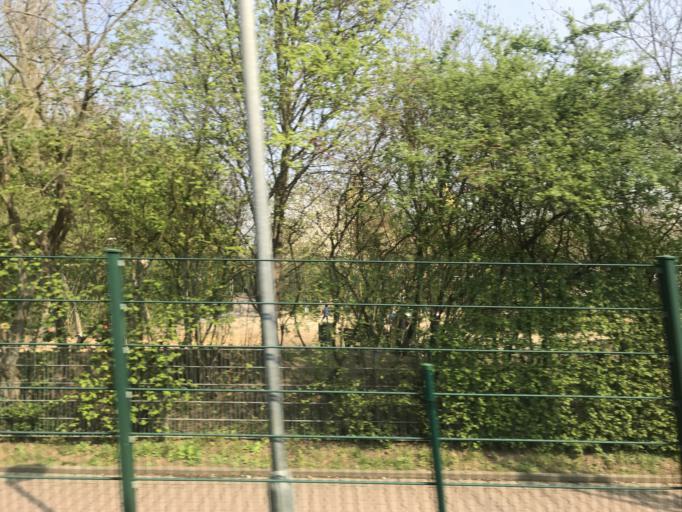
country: DE
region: Hesse
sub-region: Regierungsbezirk Darmstadt
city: Bad Homburg vor der Hoehe
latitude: 50.1658
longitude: 8.6404
